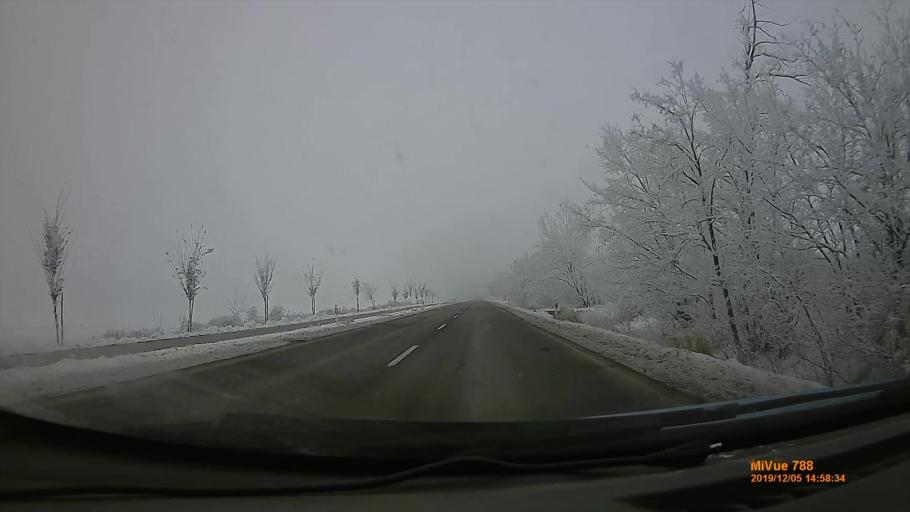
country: HU
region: Szabolcs-Szatmar-Bereg
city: Nyirtelek
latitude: 48.0496
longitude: 21.5696
